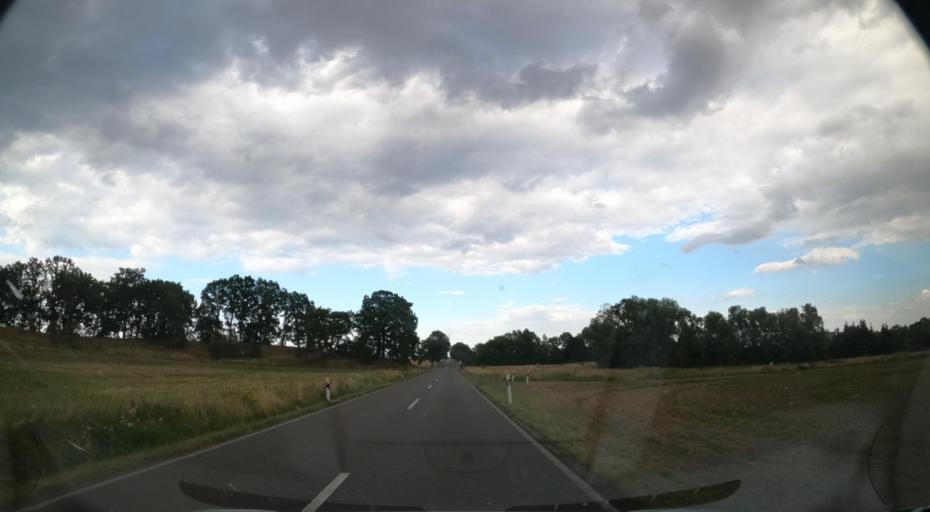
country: DE
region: Brandenburg
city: Goritz
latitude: 53.4893
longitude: 13.8709
